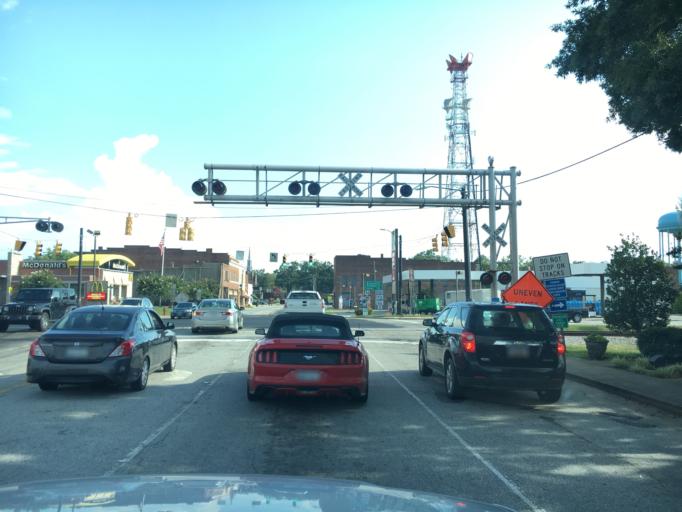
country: US
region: South Carolina
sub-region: Laurens County
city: Clinton
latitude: 34.4731
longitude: -81.8809
